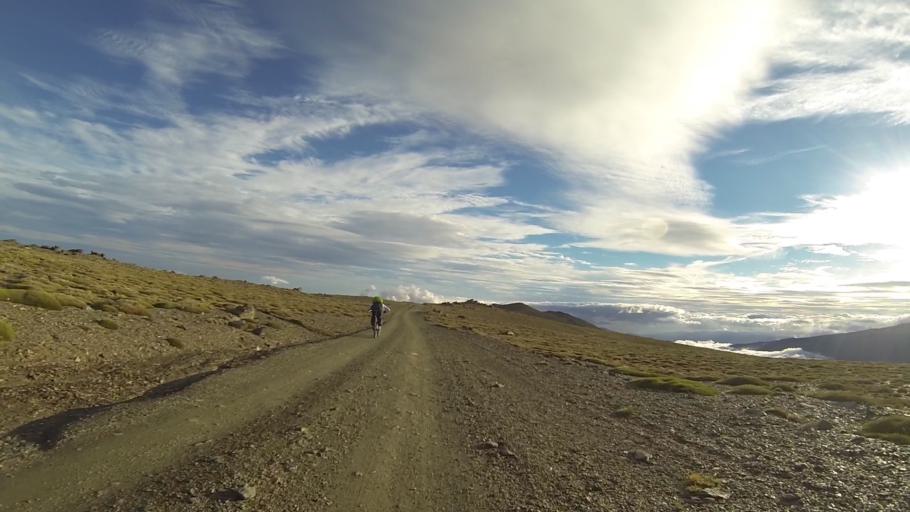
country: ES
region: Andalusia
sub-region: Provincia de Granada
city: Trevelez
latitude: 37.0054
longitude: -3.3076
